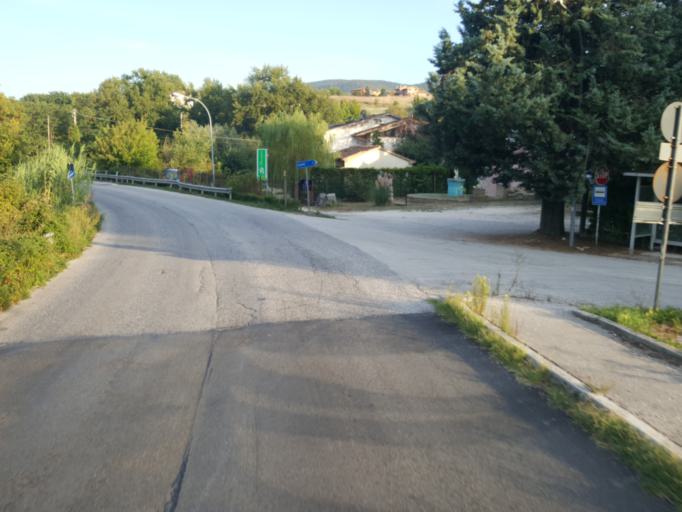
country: IT
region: The Marches
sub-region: Provincia di Ancona
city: Fabriano
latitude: 43.3473
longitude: 12.8392
